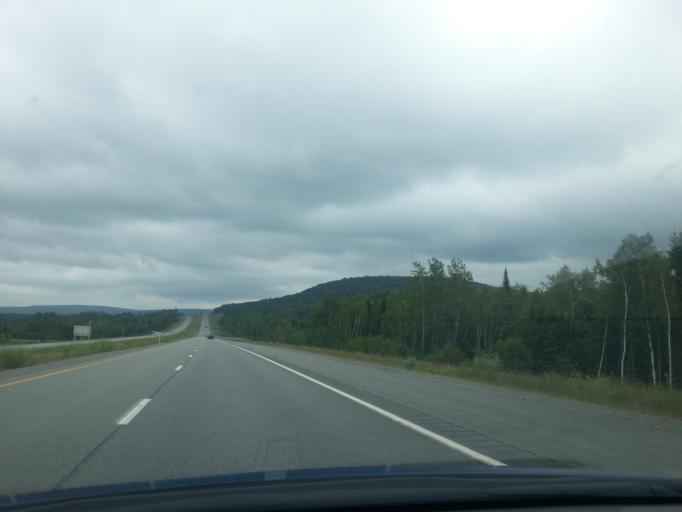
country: CA
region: New Brunswick
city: Nackawic
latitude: 45.9501
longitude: -67.3037
